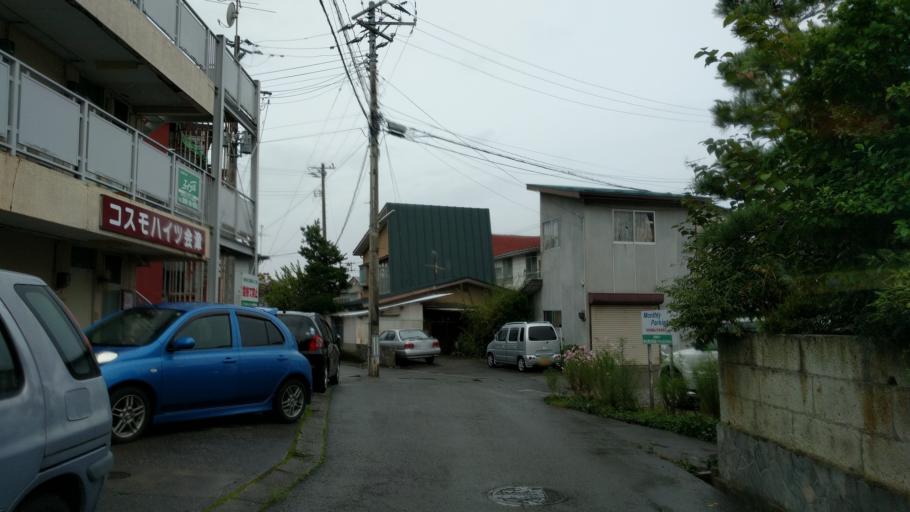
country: JP
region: Fukushima
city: Kitakata
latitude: 37.4875
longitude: 139.9466
